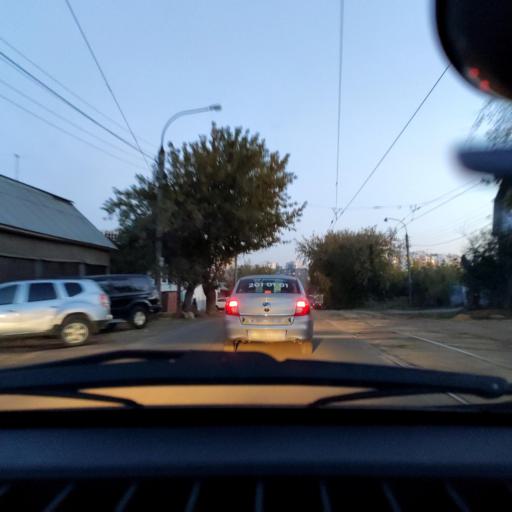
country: RU
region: Bashkortostan
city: Ufa
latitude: 54.7179
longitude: 55.9712
